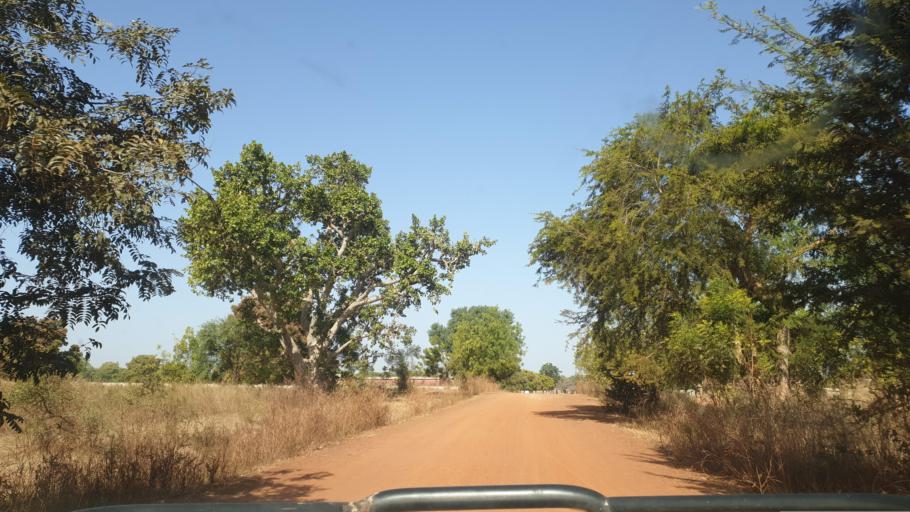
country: ML
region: Sikasso
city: Bougouni
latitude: 11.8114
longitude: -6.9338
